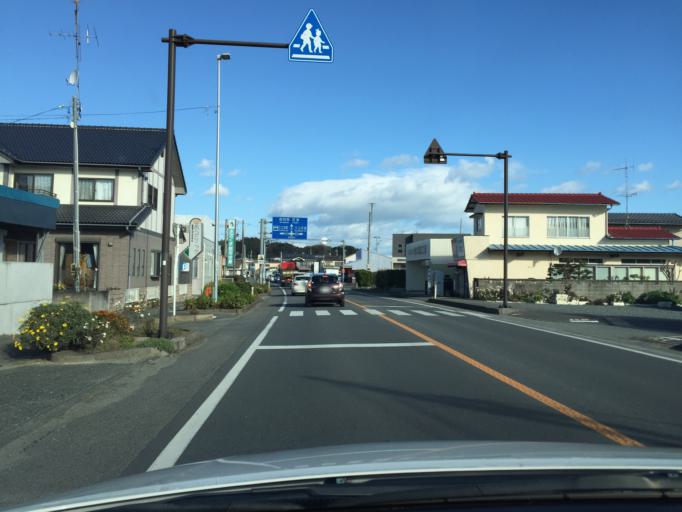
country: JP
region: Fukushima
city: Iwaki
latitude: 37.1398
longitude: 140.9969
